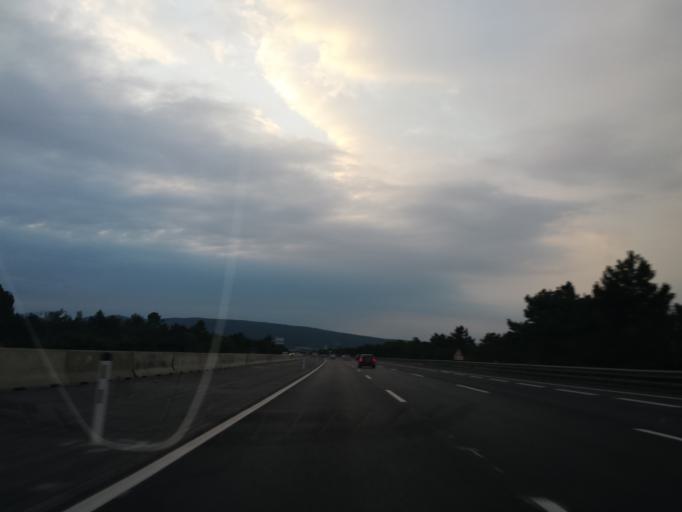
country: AT
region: Lower Austria
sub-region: Wiener Neustadt Stadt
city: Wiener Neustadt
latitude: 47.8080
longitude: 16.1981
